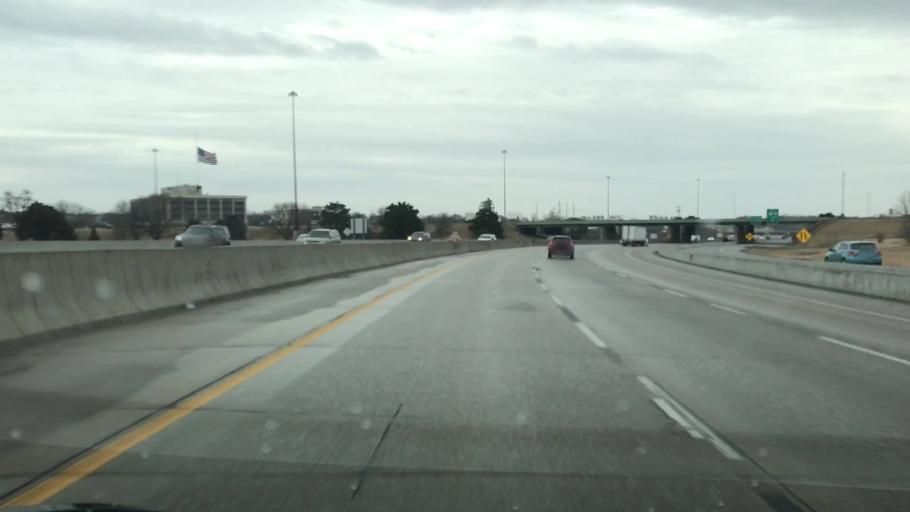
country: US
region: Nebraska
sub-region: Douglas County
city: Ralston
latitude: 41.2146
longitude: -96.0908
